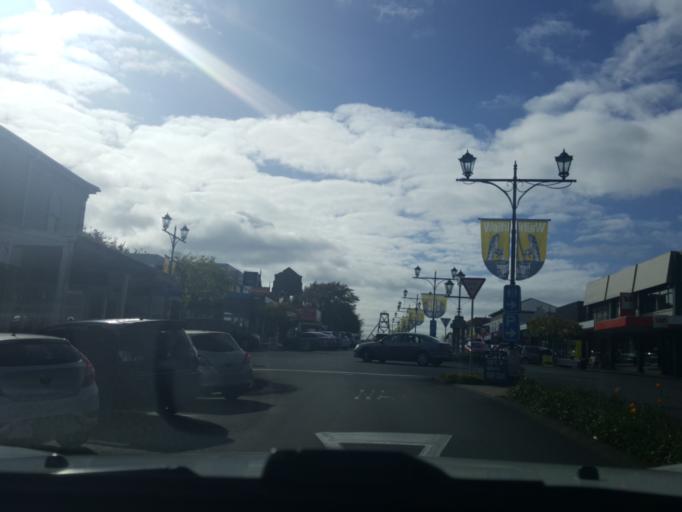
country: NZ
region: Waikato
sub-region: Hauraki District
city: Waihi
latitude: -37.3919
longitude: 175.8447
